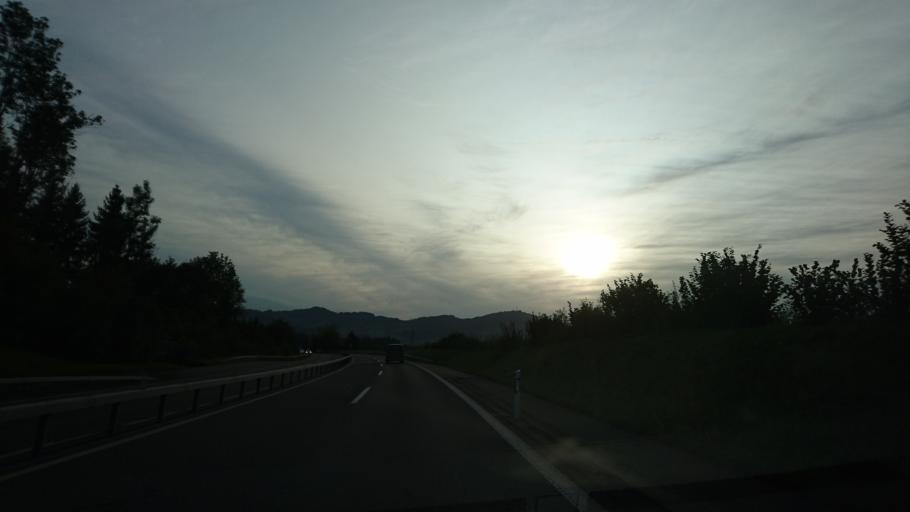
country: CH
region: Zurich
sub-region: Bezirk Hinwil
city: Bubikon
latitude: 47.2861
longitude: 8.8108
